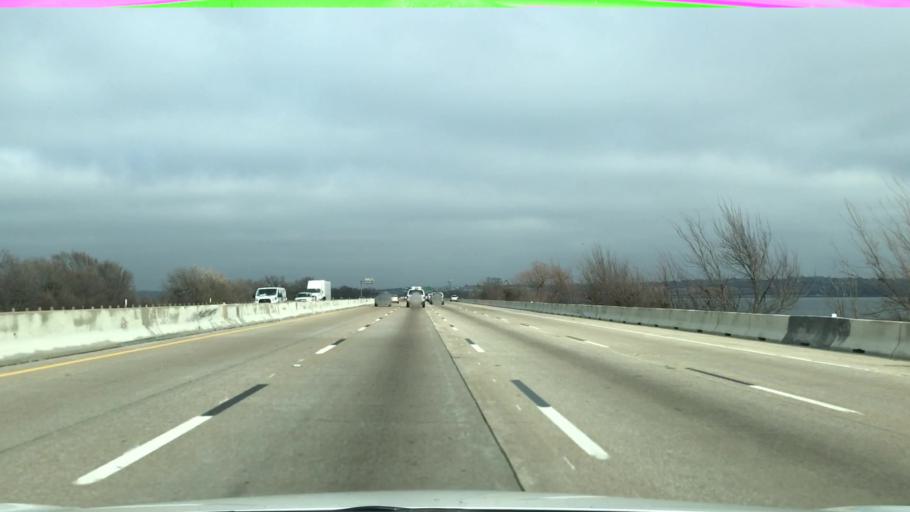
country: US
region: Texas
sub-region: Rockwall County
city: Heath
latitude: 32.8834
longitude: -96.5033
